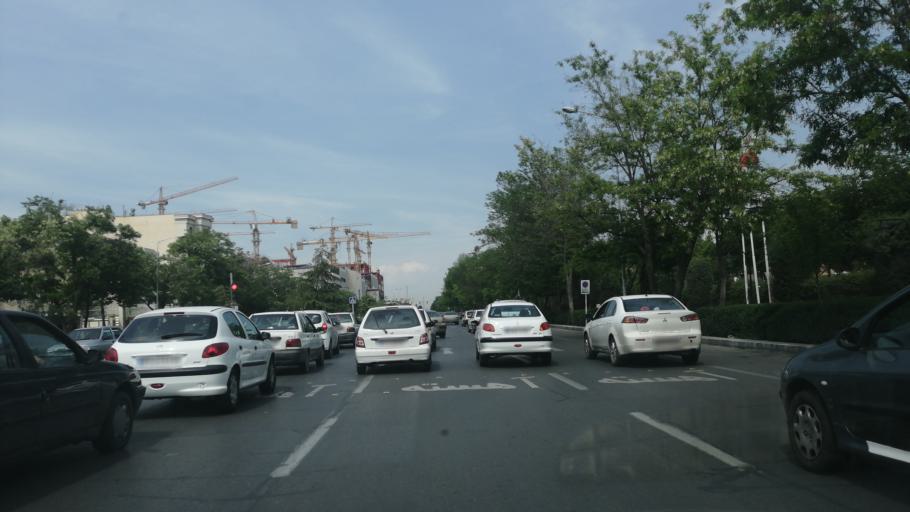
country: IR
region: Razavi Khorasan
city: Mashhad
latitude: 36.3129
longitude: 59.5583
